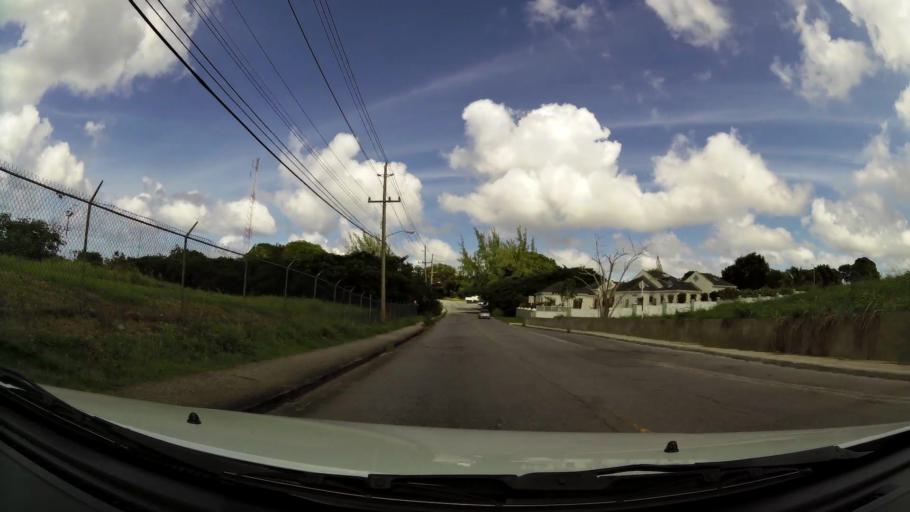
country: BB
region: Saint James
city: Holetown
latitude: 13.1474
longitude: -59.6231
